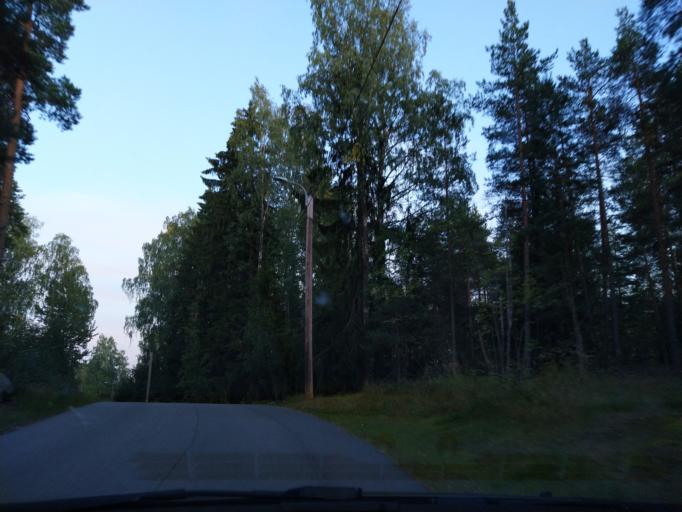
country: FI
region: Uusimaa
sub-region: Helsinki
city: Tuusula
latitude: 60.3623
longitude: 25.0589
